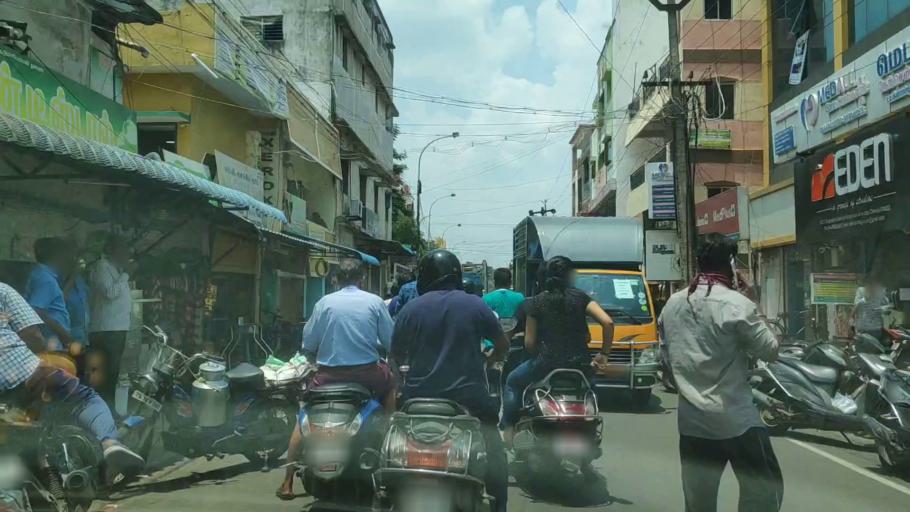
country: IN
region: Tamil Nadu
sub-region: Thiruvallur
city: Ambattur
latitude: 13.1211
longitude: 80.1514
